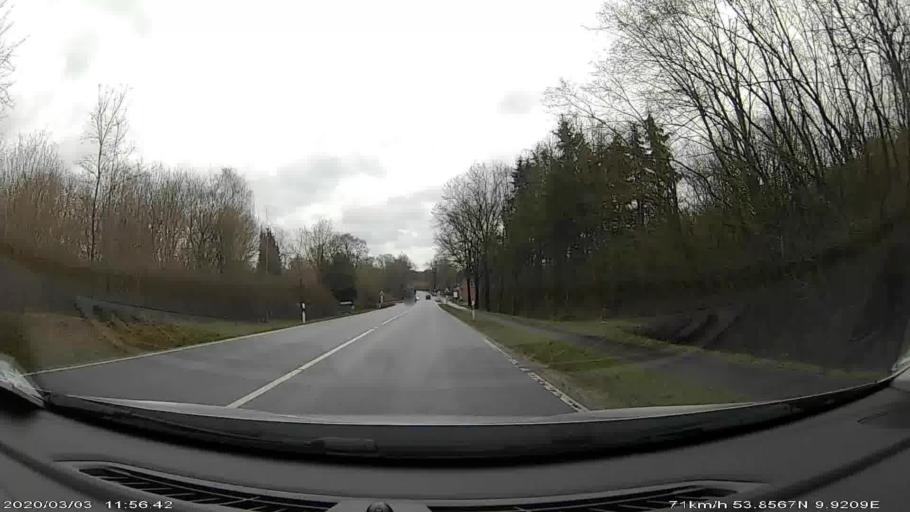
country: DE
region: Schleswig-Holstein
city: Nutzen
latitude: 53.8556
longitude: 9.9237
